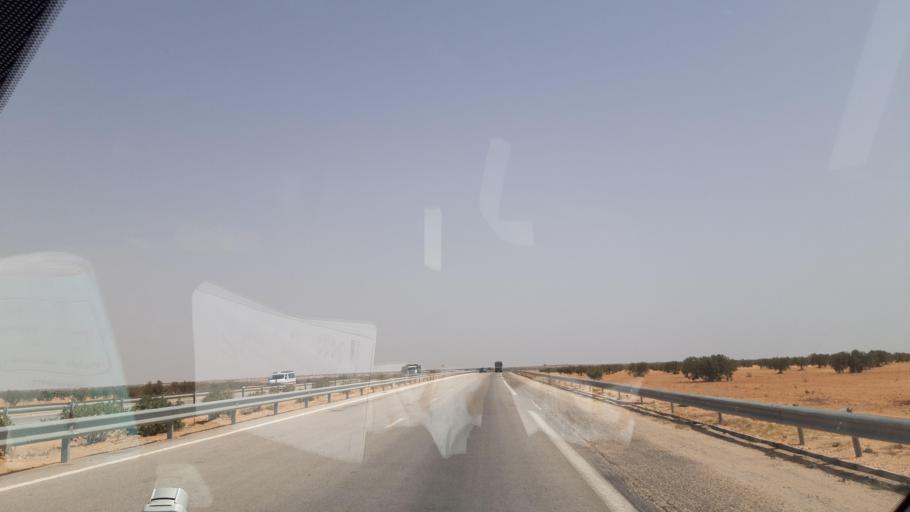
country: TN
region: Safaqis
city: Bi'r `Ali Bin Khalifah
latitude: 34.5281
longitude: 10.1220
